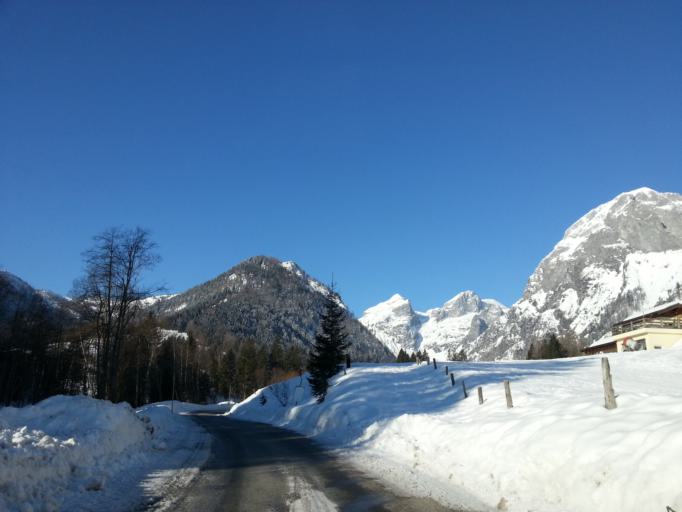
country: AT
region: Salzburg
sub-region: Politischer Bezirk Hallein
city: Abtenau
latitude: 47.4993
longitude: 13.3768
